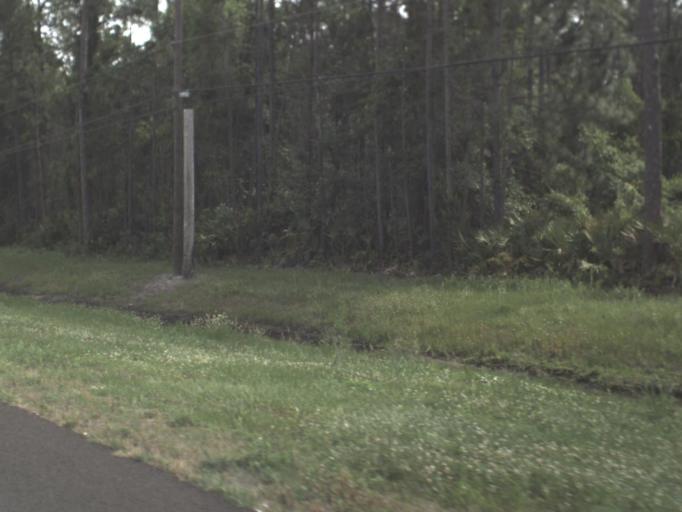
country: US
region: Florida
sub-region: Saint Johns County
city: Fruit Cove
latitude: 30.0950
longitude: -81.7059
